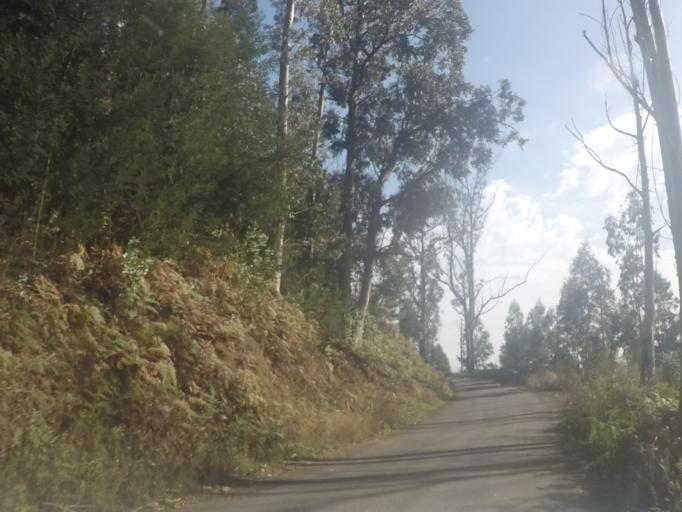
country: PT
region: Madeira
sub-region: Funchal
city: Nossa Senhora do Monte
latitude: 32.6907
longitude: -16.9076
